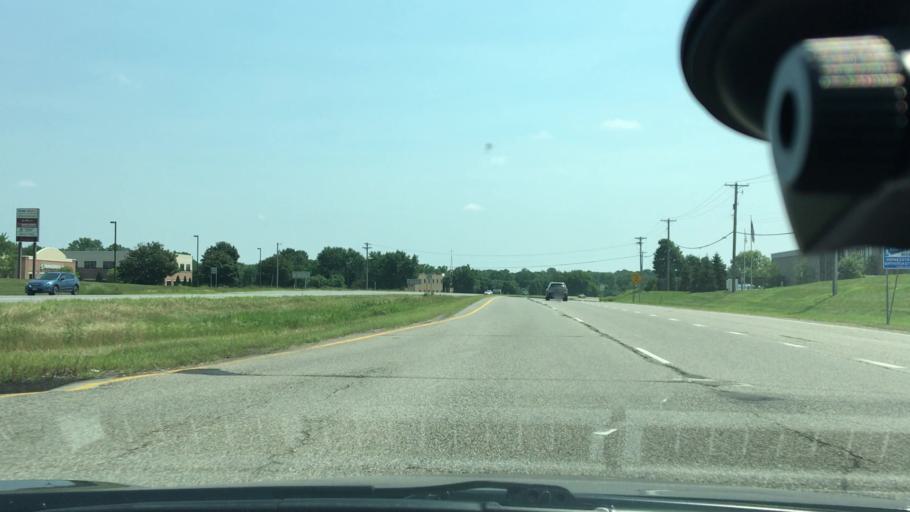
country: US
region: Minnesota
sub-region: Hennepin County
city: Plymouth
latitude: 45.0081
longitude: -93.4507
